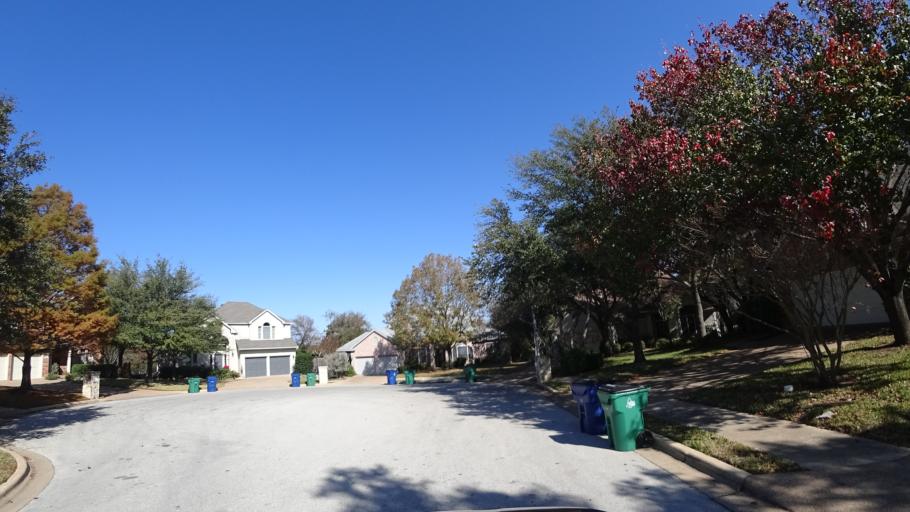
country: US
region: Texas
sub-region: Travis County
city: Lost Creek
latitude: 30.3741
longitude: -97.8434
